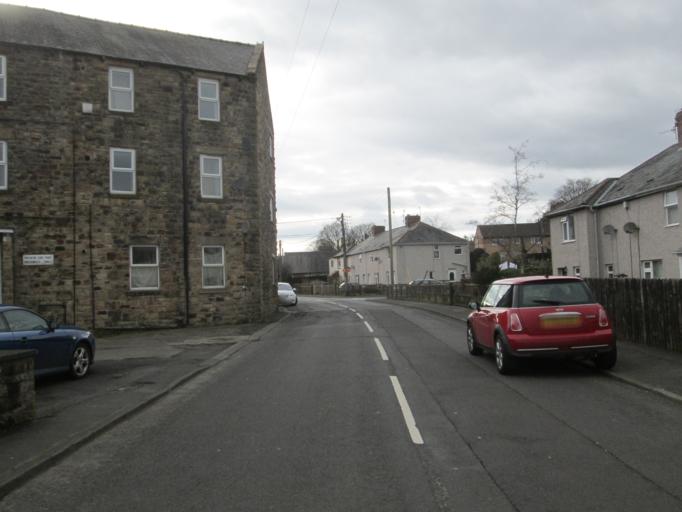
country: GB
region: England
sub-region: Northumberland
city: Haltwhistle
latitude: 54.9690
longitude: -2.4668
